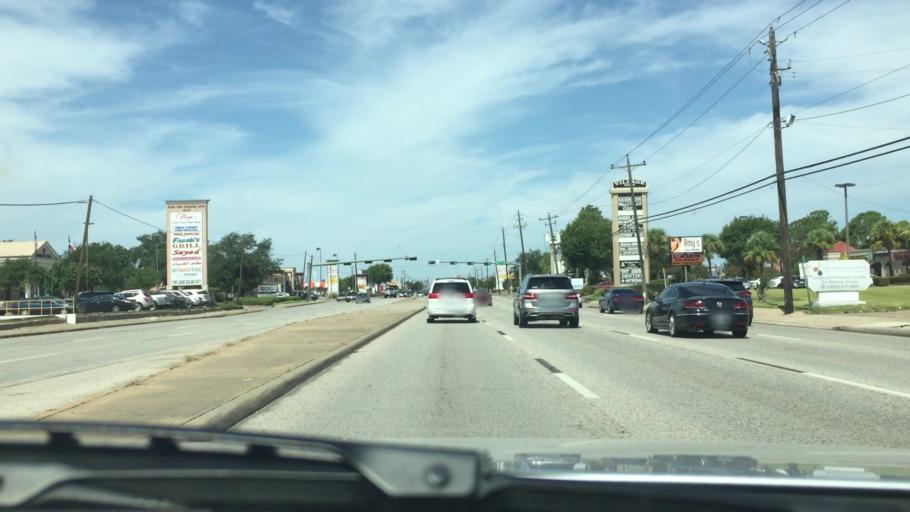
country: US
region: Texas
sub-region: Harris County
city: Bunker Hill Village
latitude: 29.7363
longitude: -95.5963
